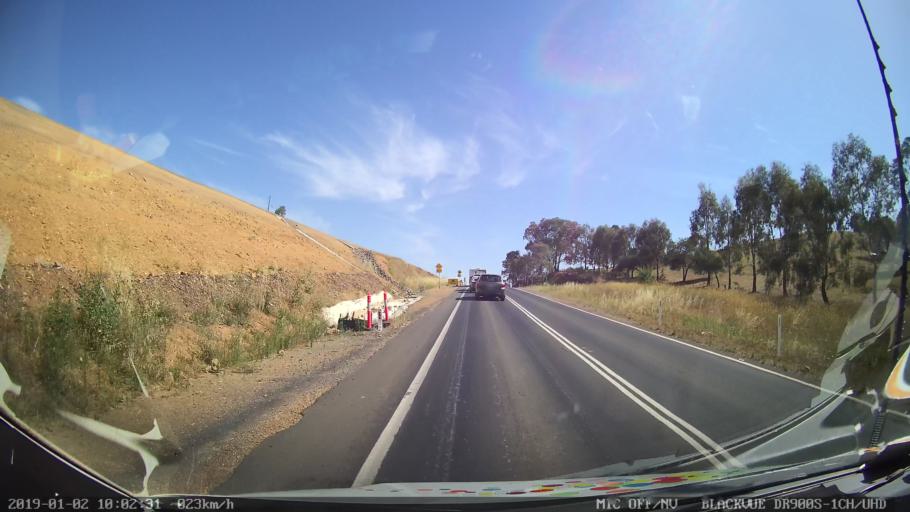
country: AU
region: New South Wales
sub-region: Gundagai
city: Gundagai
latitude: -35.1827
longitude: 148.1263
